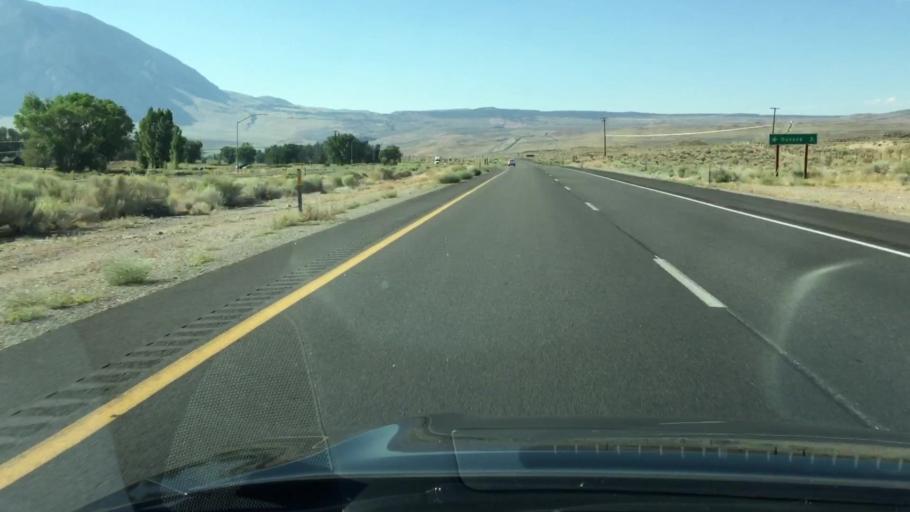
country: US
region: California
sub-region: Inyo County
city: West Bishop
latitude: 37.4171
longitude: -118.5539
